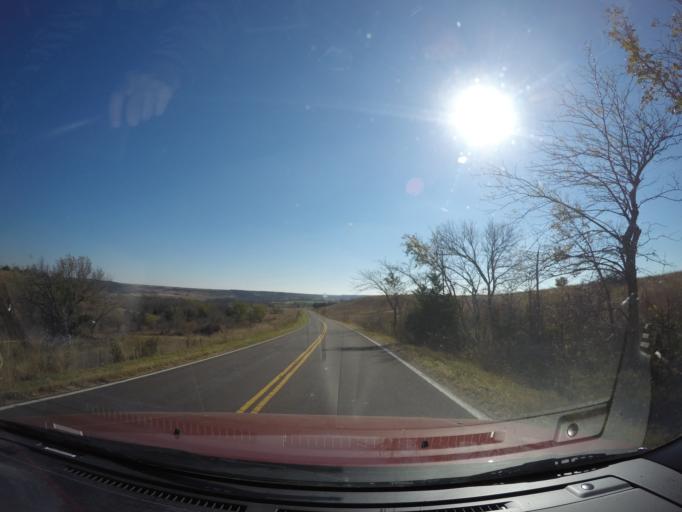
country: US
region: Kansas
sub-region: Geary County
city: Grandview Plaza
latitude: 39.0114
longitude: -96.7521
